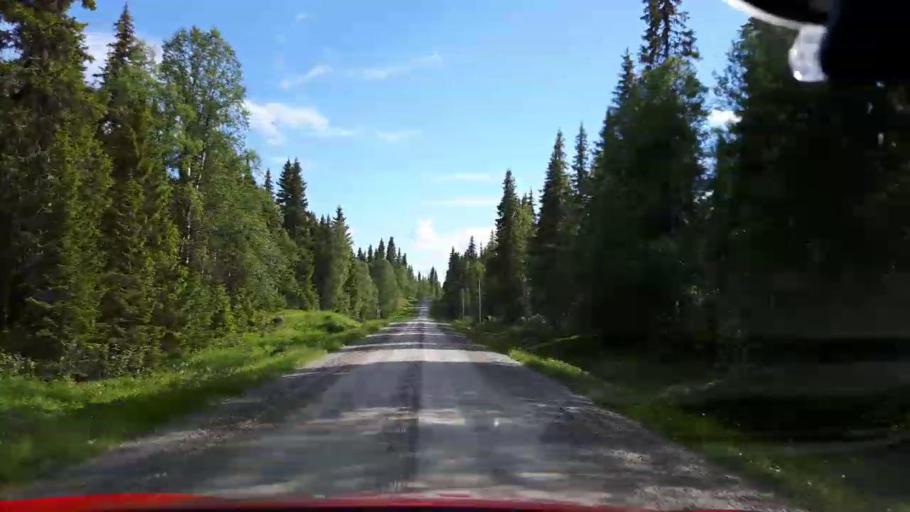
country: SE
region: Jaemtland
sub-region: Krokoms Kommun
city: Valla
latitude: 63.7970
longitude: 14.0461
